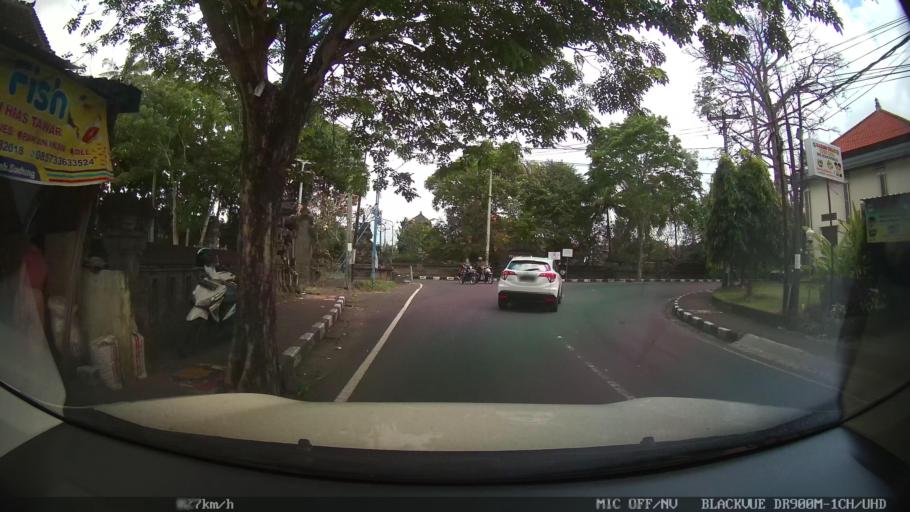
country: ID
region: Bali
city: Banjar Karangsuling
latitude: -8.5972
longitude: 115.1741
